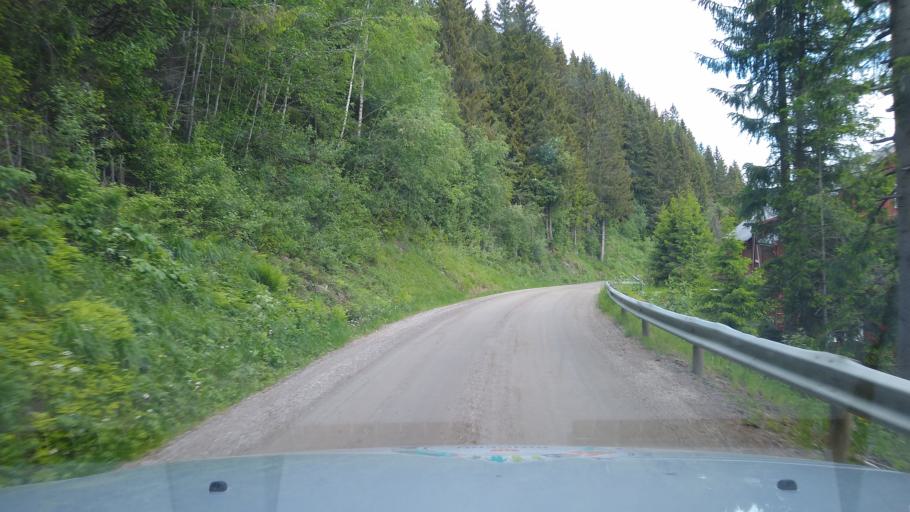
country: NO
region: Oppland
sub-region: Ringebu
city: Ringebu
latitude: 61.5013
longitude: 10.1397
